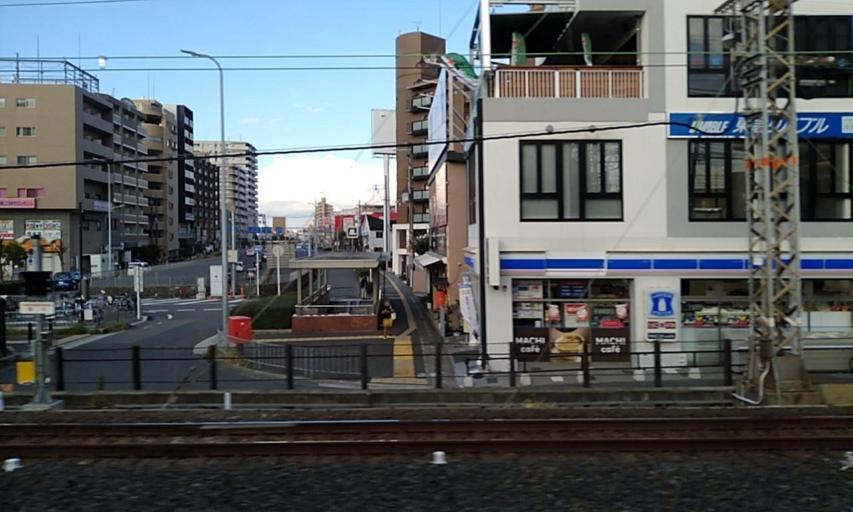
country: JP
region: Osaka
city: Matsubara
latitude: 34.5554
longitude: 135.5055
